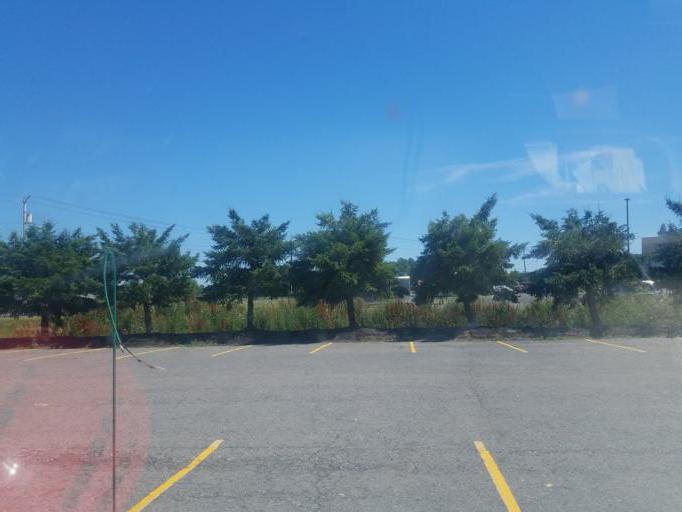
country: US
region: New York
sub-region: Ontario County
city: Geneva
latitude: 42.8561
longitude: -77.0113
